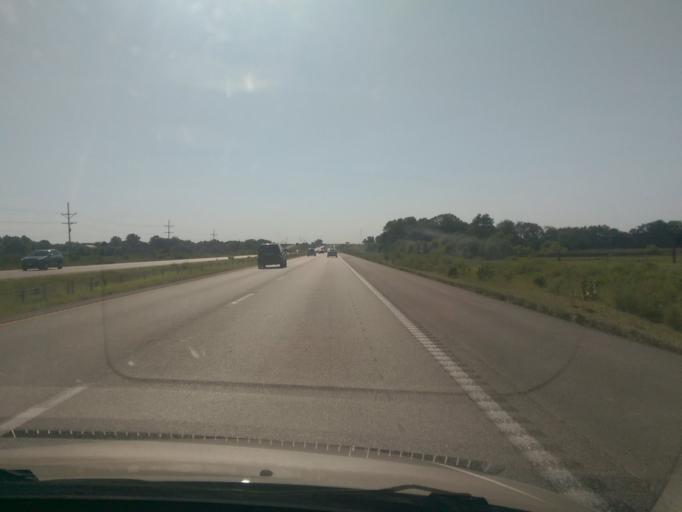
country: US
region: Missouri
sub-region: Saline County
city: Sweet Springs
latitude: 38.9782
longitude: -93.4459
